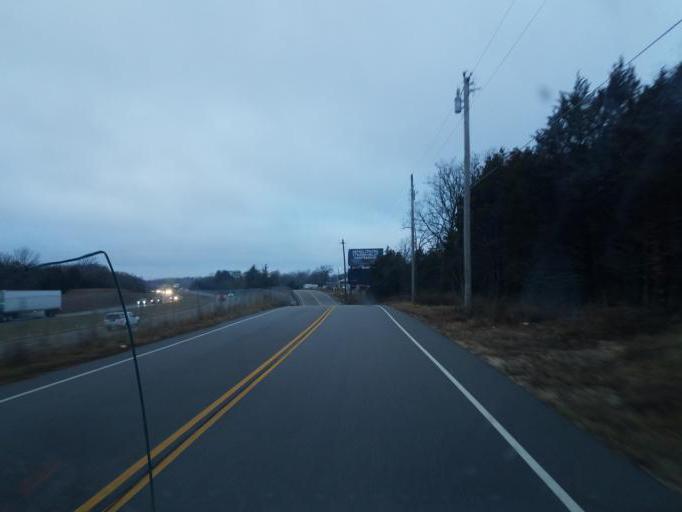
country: US
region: Missouri
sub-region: Phelps County
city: Rolla
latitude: 37.9766
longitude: -91.7418
